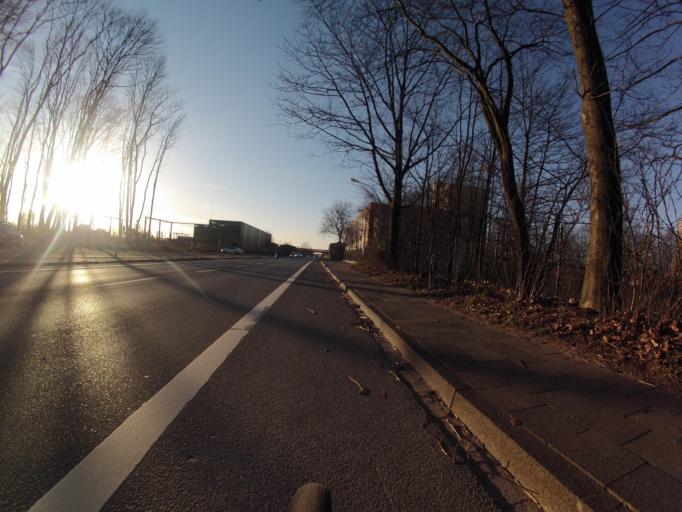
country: DE
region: North Rhine-Westphalia
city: Ibbenburen
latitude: 52.2856
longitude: 7.7427
